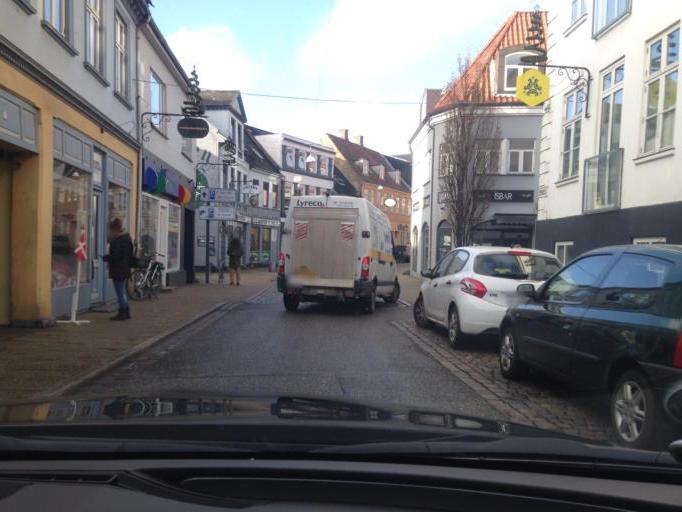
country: DK
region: South Denmark
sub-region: Kolding Kommune
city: Kolding
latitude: 55.4920
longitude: 9.4712
